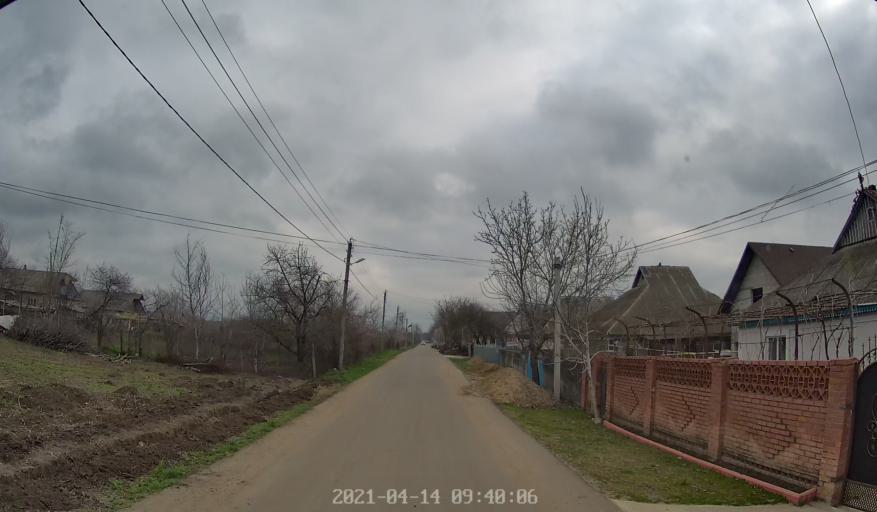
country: MD
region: Chisinau
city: Vadul lui Voda
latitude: 47.1339
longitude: 29.1251
